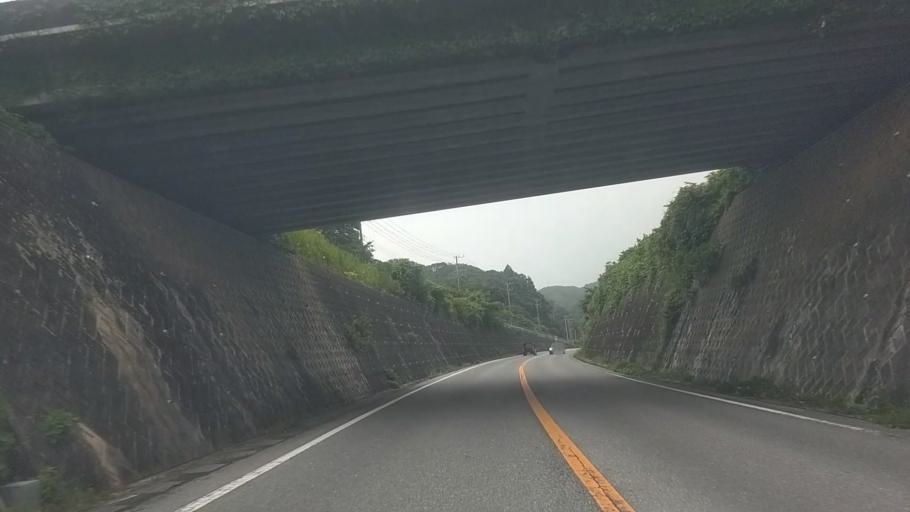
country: JP
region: Chiba
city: Katsuura
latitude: 35.1588
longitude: 140.3158
